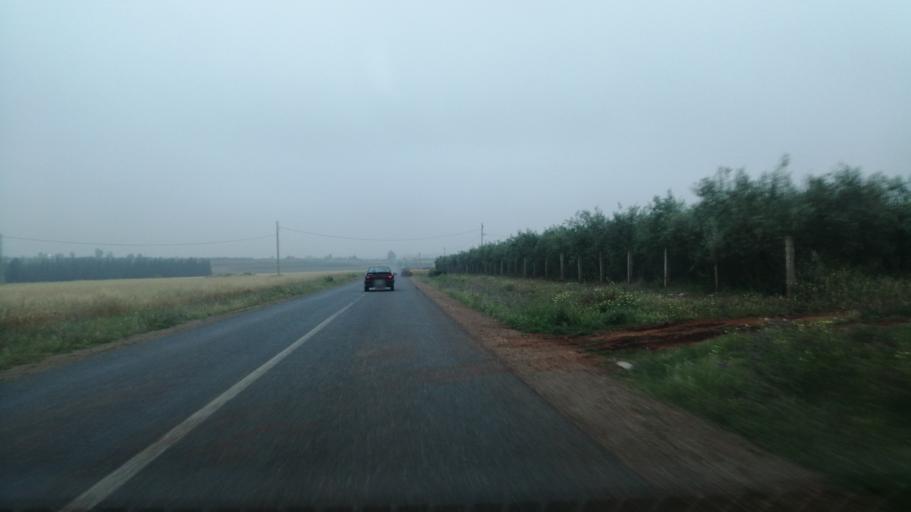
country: MA
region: Rabat-Sale-Zemmour-Zaer
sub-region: Khemisset
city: Tiflet
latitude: 33.7449
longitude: -6.2686
